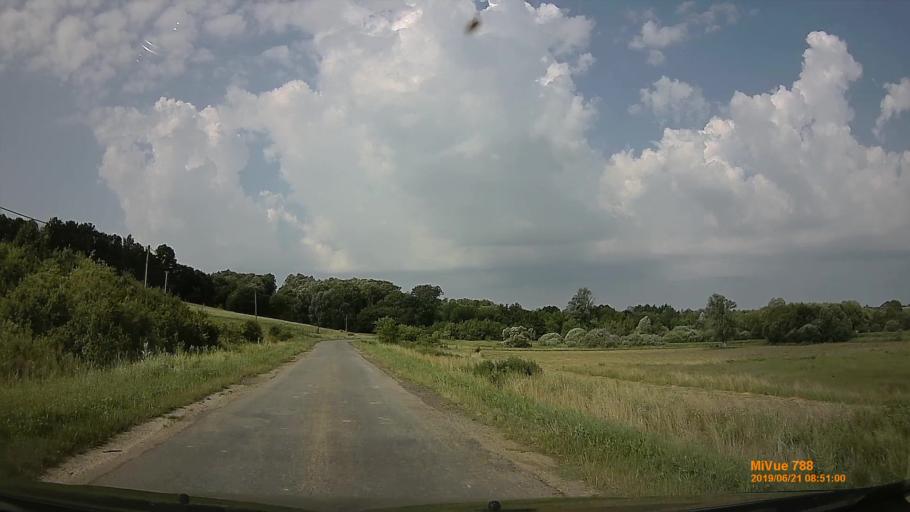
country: HU
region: Baranya
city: Buekkoesd
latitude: 46.1741
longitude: 17.9127
